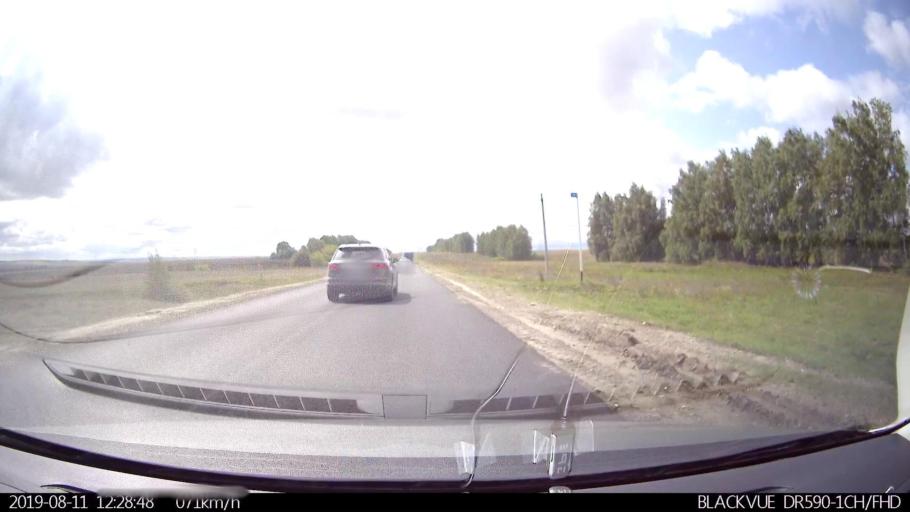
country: RU
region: Ulyanovsk
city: Ignatovka
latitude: 53.8402
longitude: 47.9086
